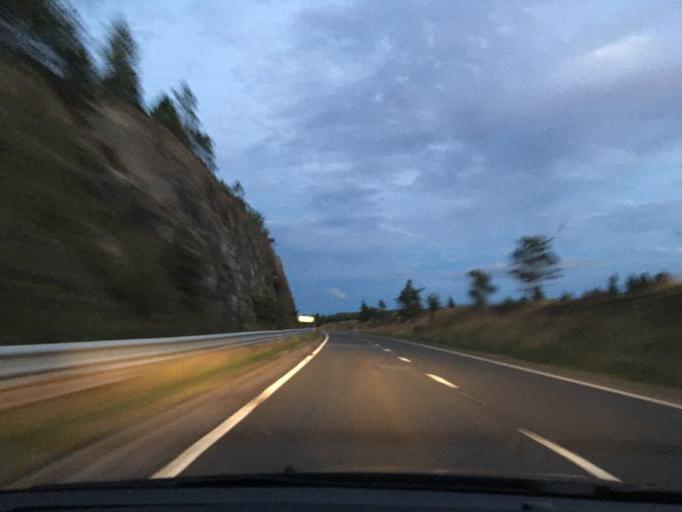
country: GB
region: Scotland
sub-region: Highland
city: Kingussie
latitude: 56.8086
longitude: -4.1010
